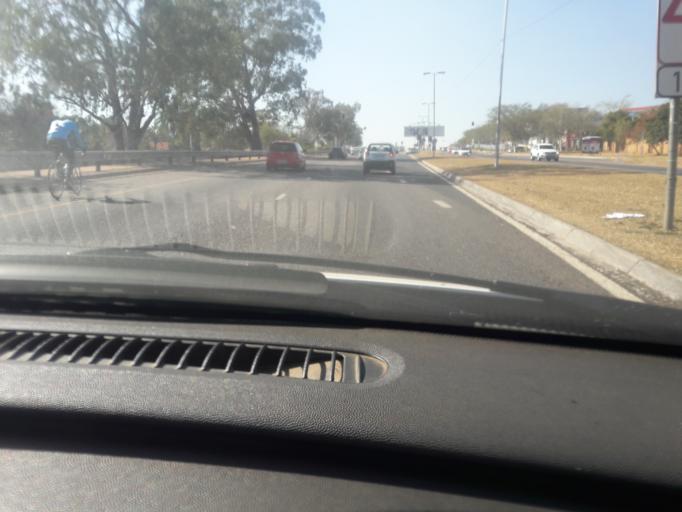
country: ZA
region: Gauteng
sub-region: City of Tshwane Metropolitan Municipality
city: Pretoria
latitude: -25.7671
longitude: 28.2934
